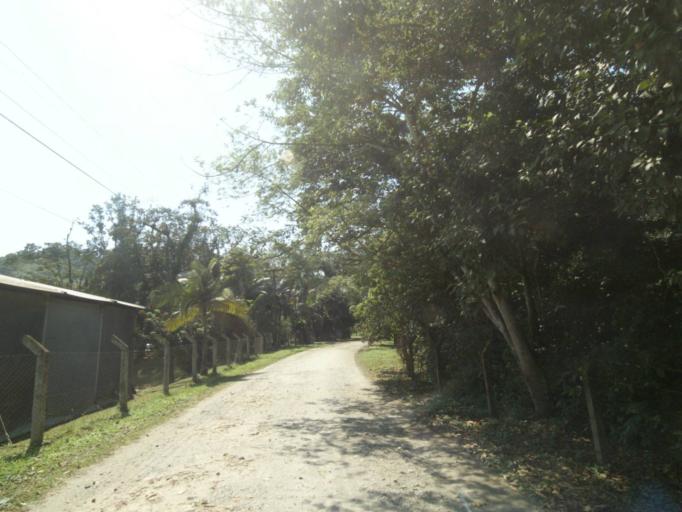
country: BR
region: Parana
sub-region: Paranagua
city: Paranagua
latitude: -25.5499
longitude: -48.5908
